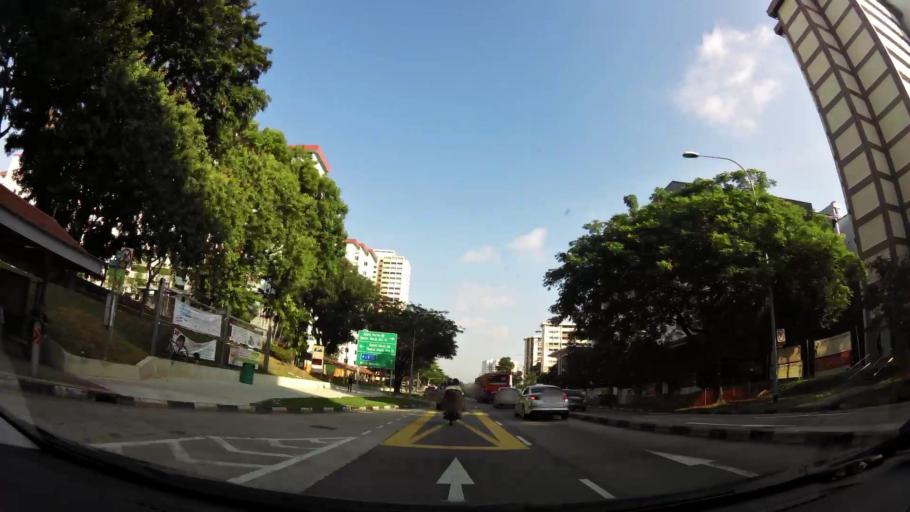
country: SG
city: Singapore
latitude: 1.3301
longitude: 103.9345
